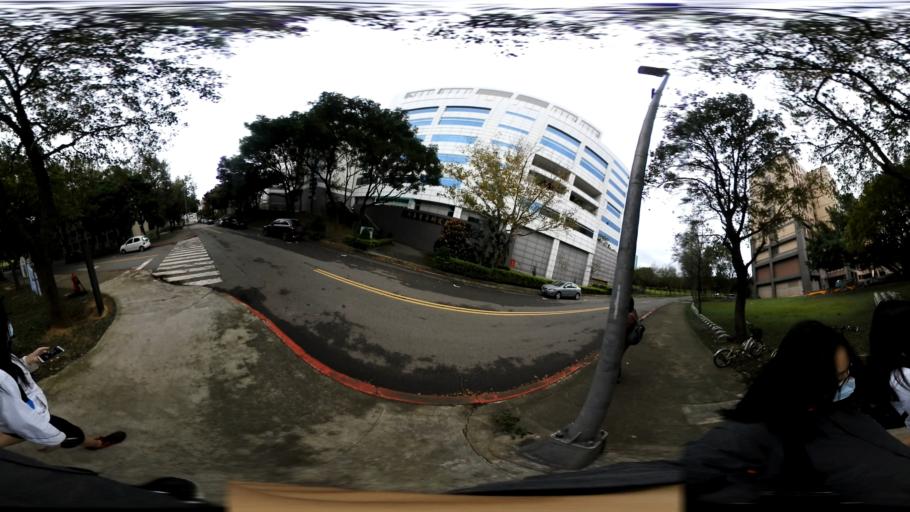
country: TW
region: Taiwan
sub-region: Hsinchu
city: Hsinchu
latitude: 24.7847
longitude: 121.0003
